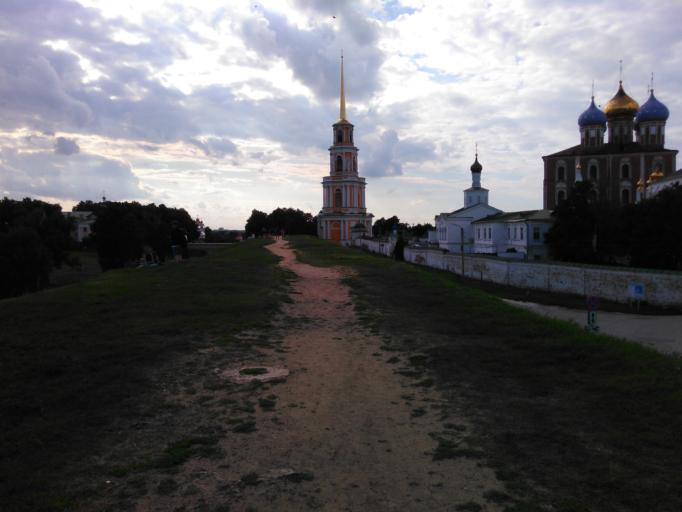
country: RU
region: Rjazan
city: Ryazan'
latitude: 54.6347
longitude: 39.7513
